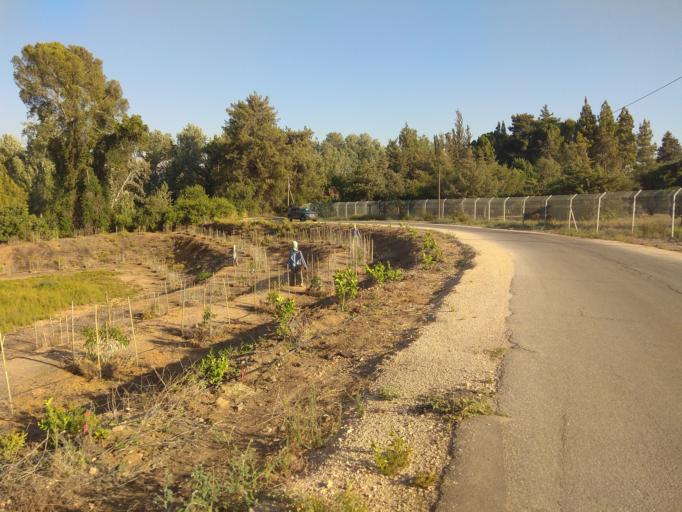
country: IL
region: Northern District
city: Qiryat Shemona
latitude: 33.2230
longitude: 35.6189
